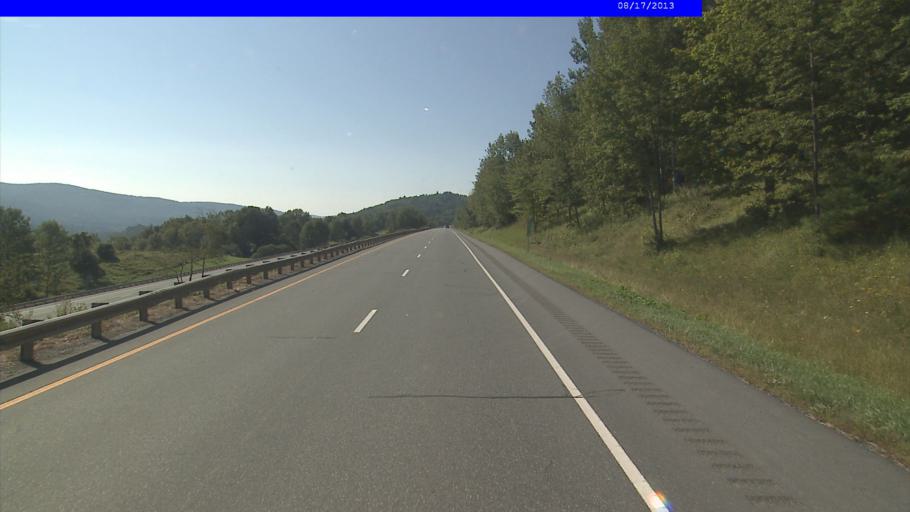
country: US
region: Vermont
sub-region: Windsor County
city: Windsor
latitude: 43.5177
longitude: -72.4089
